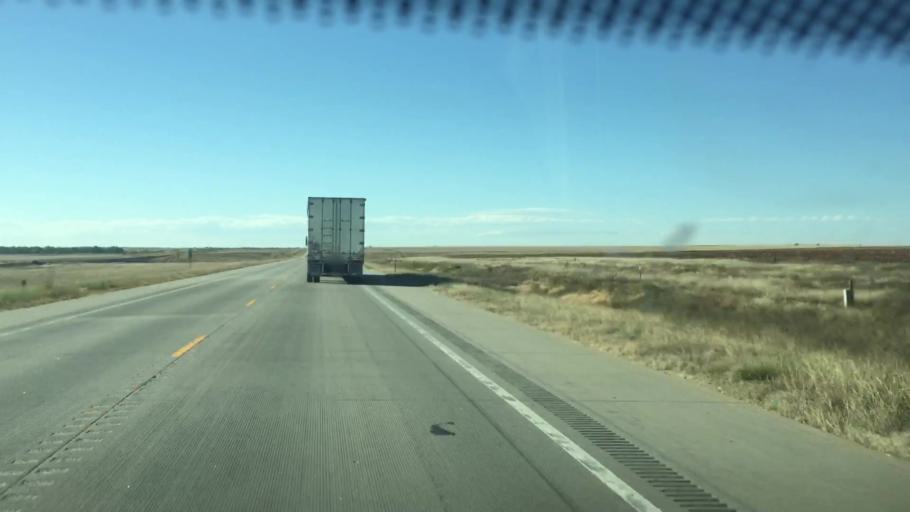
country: US
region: Colorado
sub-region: Kiowa County
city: Eads
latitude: 38.8000
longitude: -102.9557
